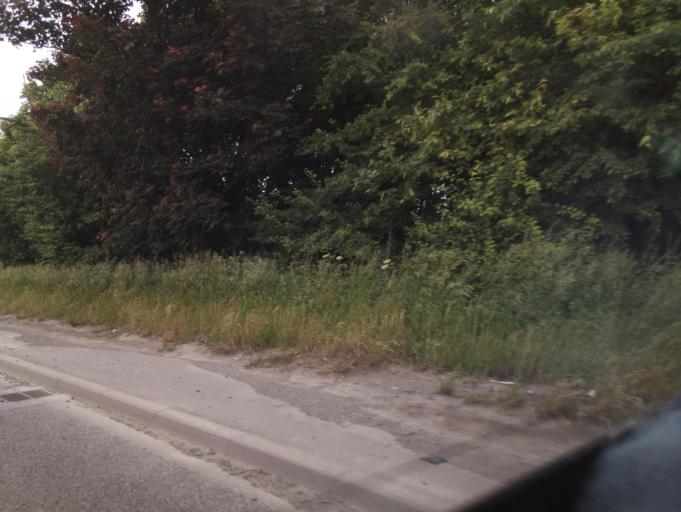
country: GB
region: England
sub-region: Leicestershire
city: Markfield
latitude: 52.7022
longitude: -1.3187
